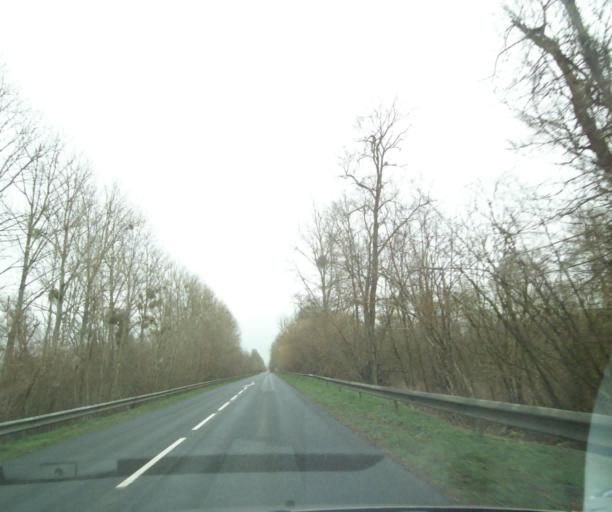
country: FR
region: Picardie
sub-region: Departement de l'Oise
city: Noyon
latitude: 49.5631
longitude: 3.0312
